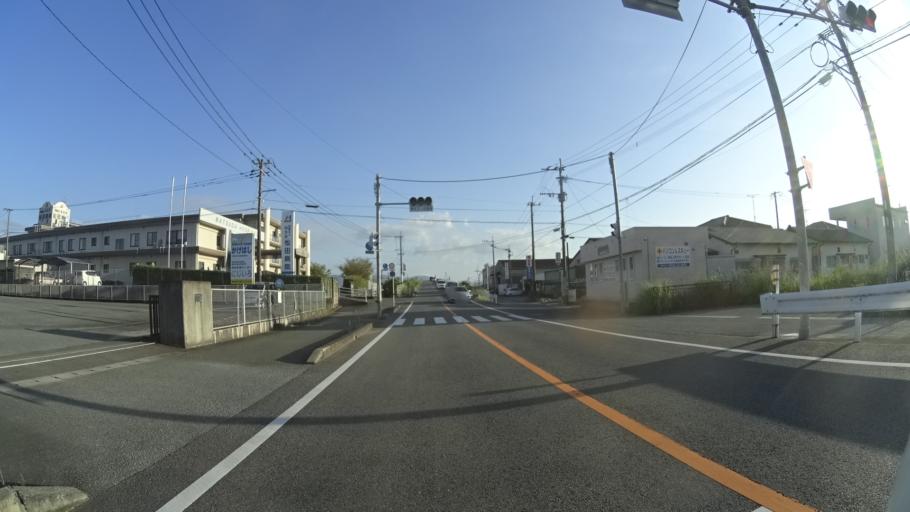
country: JP
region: Kumamoto
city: Matsubase
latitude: 32.6444
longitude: 130.6753
